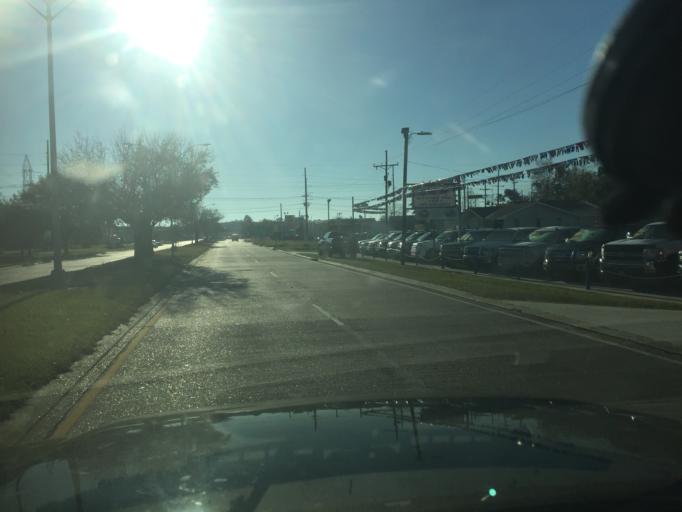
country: US
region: Louisiana
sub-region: Saint Tammany Parish
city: Slidell
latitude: 30.2506
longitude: -89.7663
